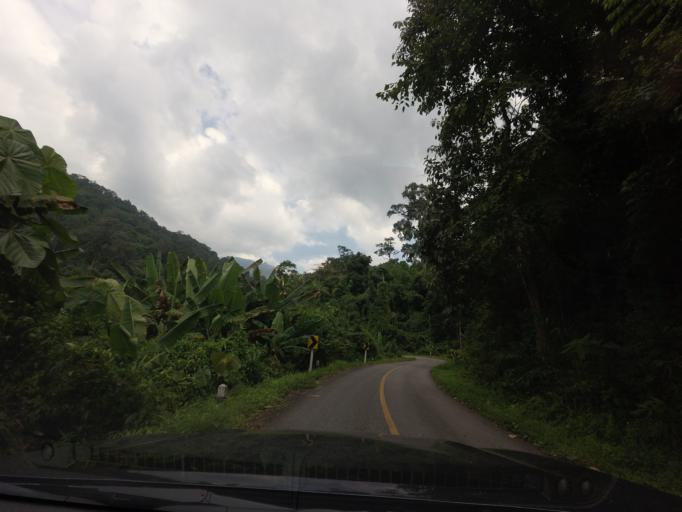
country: TH
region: Loei
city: Na Haeo
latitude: 17.7045
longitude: 100.9497
